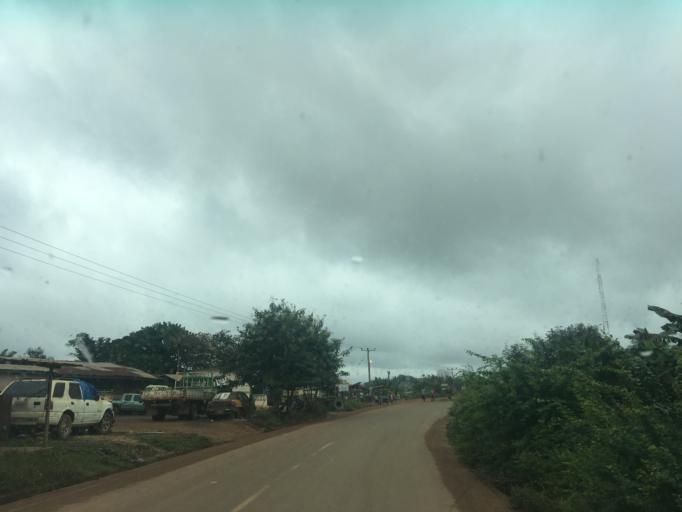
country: GH
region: Western
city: Wassa-Akropong
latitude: 5.8144
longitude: -2.4339
